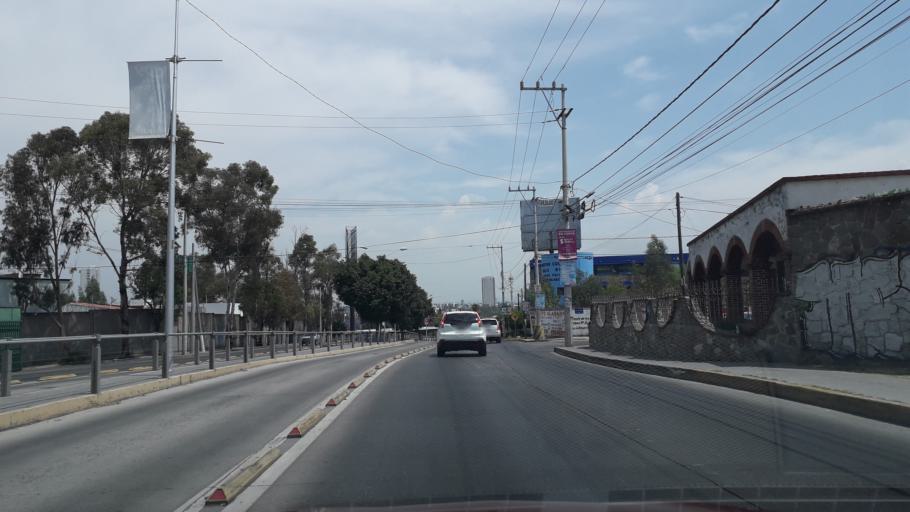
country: MX
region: Puebla
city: Puebla
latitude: 19.0160
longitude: -98.2314
